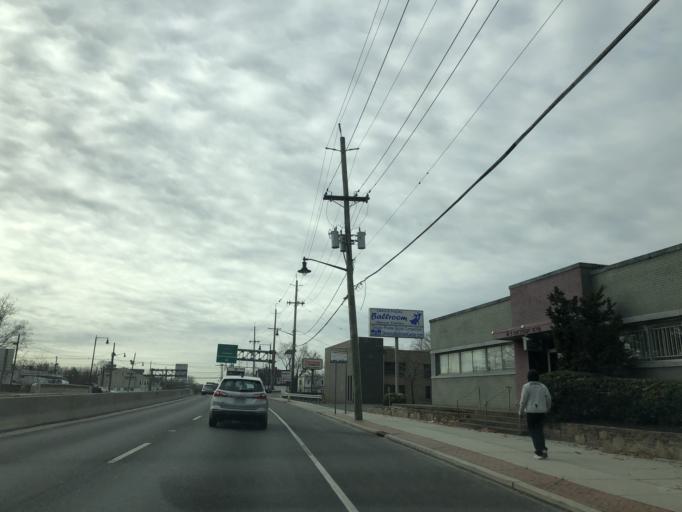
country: US
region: New Jersey
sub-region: Camden County
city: Wood-Lynne
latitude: 39.9236
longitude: -75.0859
